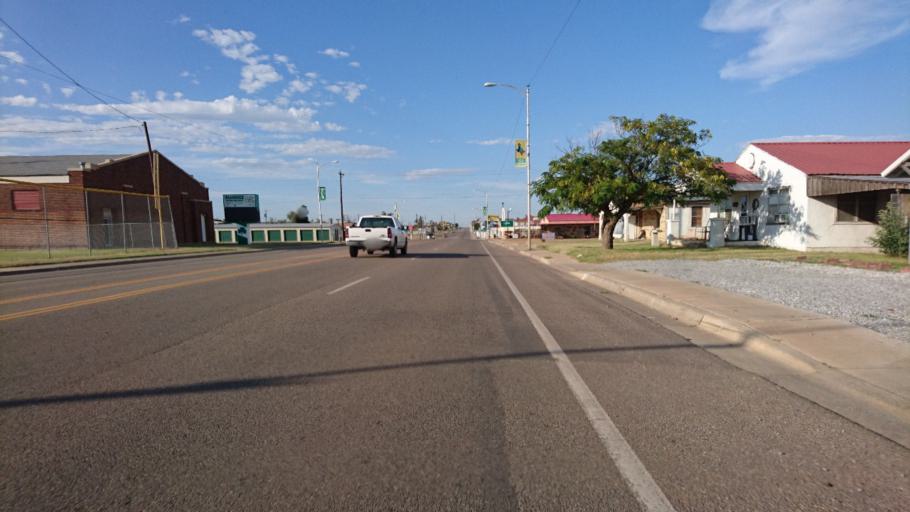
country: US
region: Texas
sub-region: Wheeler County
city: Shamrock
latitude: 35.2243
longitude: -100.2492
